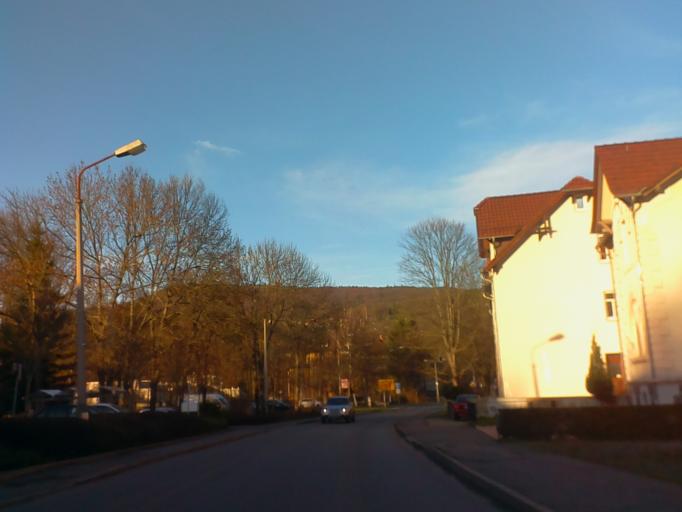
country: DE
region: Thuringia
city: Bad Blankenburg
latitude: 50.6805
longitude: 11.2732
